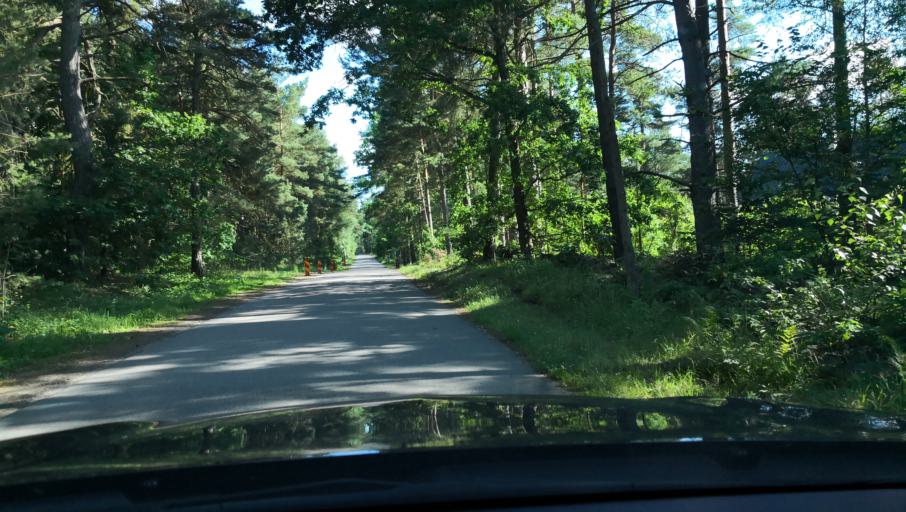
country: SE
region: Skane
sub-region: Simrishamns Kommun
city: Kivik
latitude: 55.7806
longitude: 14.1939
